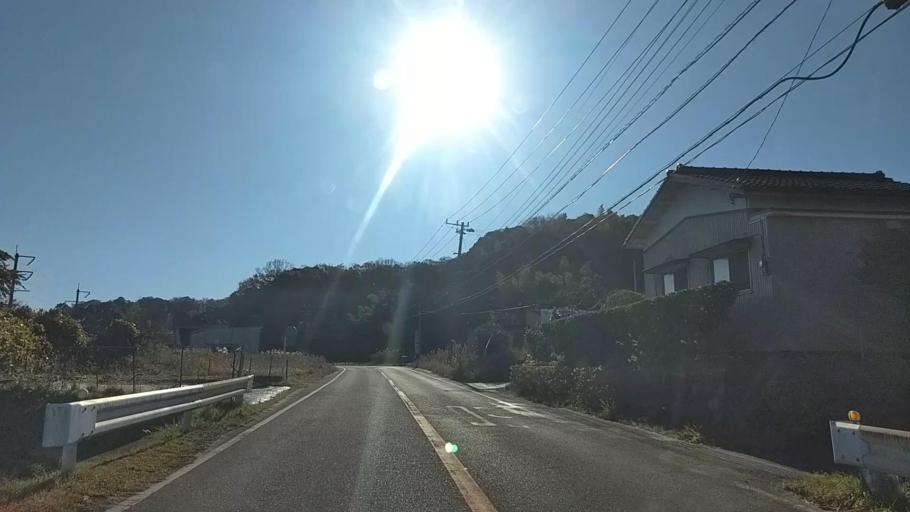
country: JP
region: Chiba
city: Futtsu
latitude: 35.2706
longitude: 139.8650
